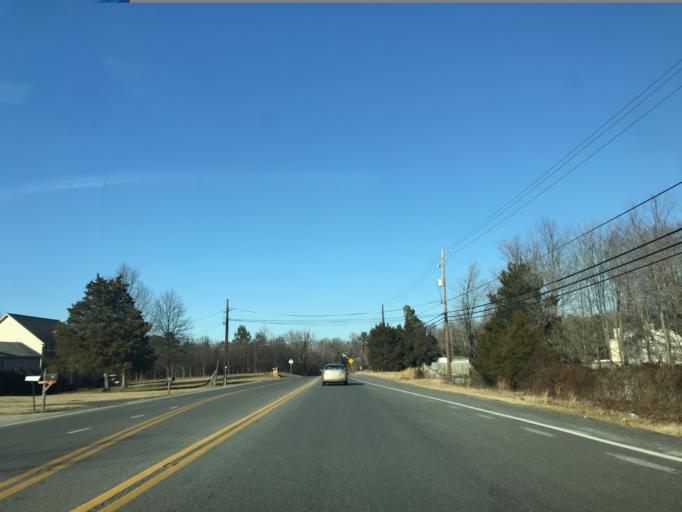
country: US
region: Maryland
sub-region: Prince George's County
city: Friendly
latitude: 38.7242
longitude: -76.9523
